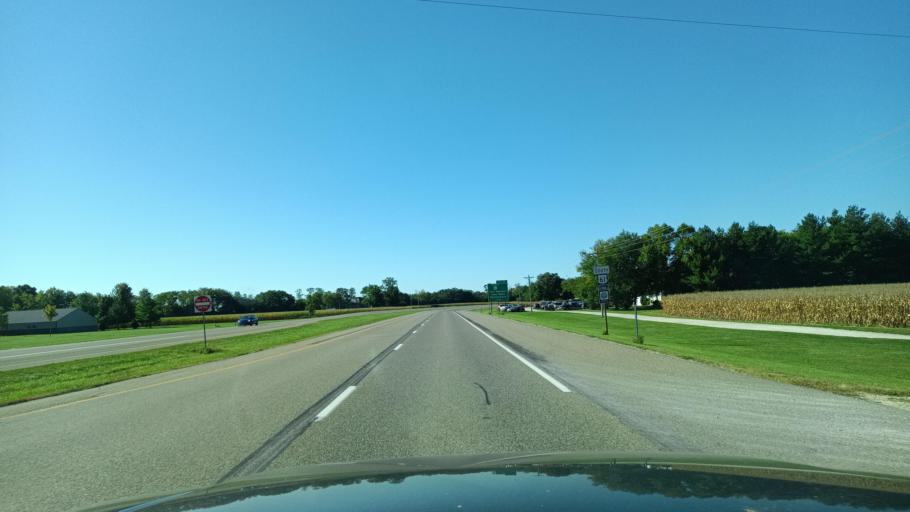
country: US
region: Iowa
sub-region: Lee County
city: Fort Madison
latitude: 40.6842
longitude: -91.2512
